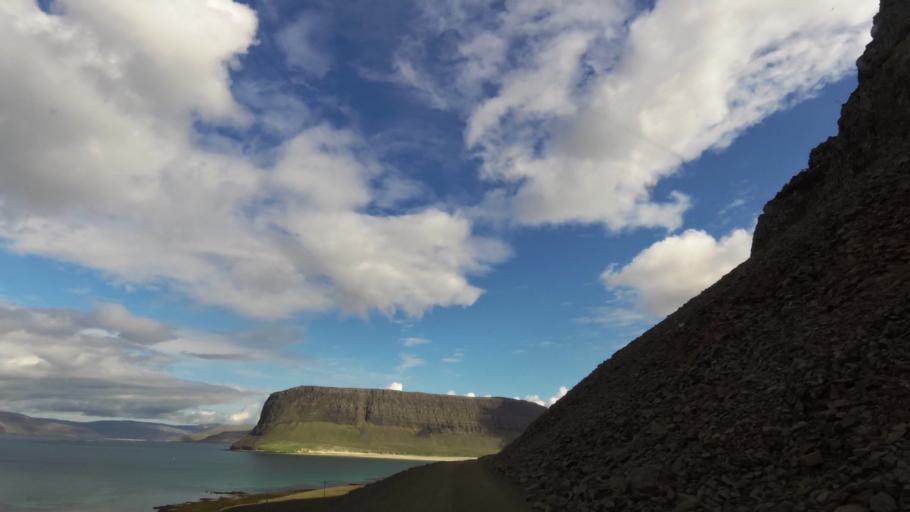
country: IS
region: West
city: Olafsvik
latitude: 65.5964
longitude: -24.1312
